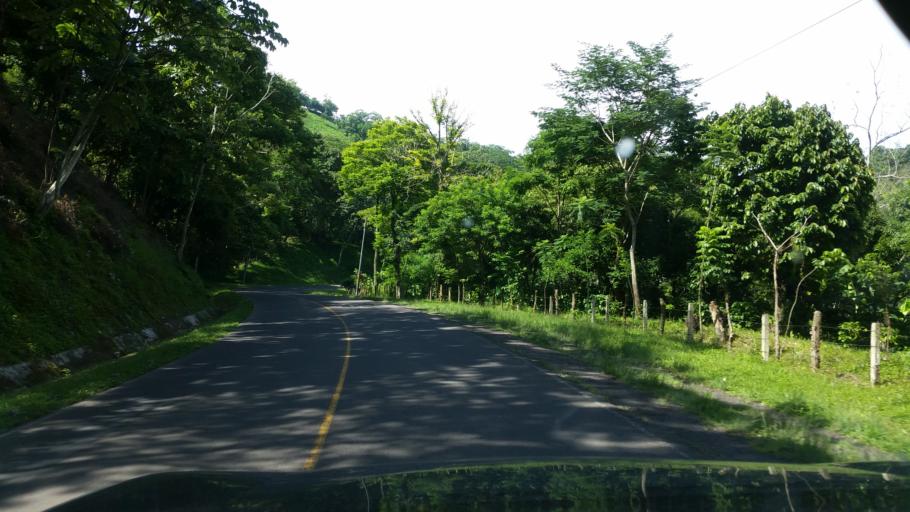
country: NI
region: Matagalpa
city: San Ramon
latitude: 13.0138
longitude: -85.7971
